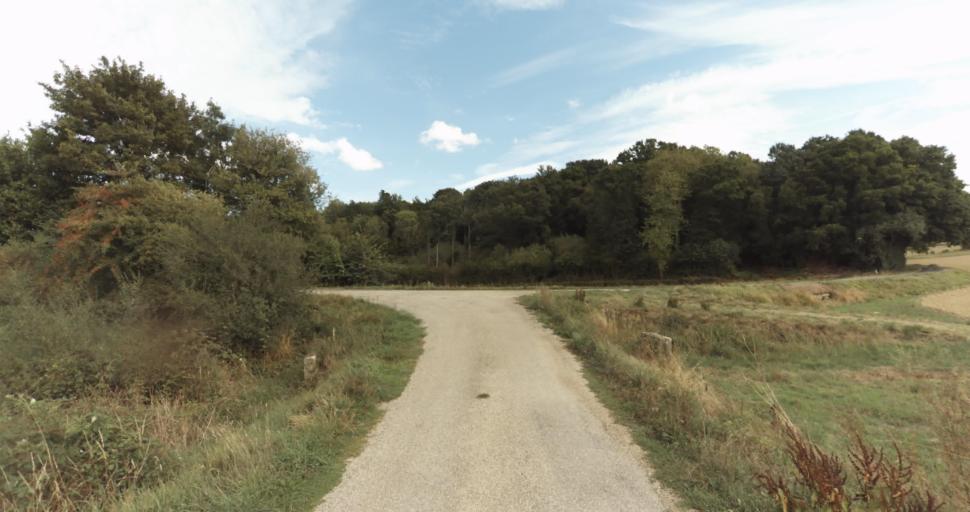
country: FR
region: Lower Normandy
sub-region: Departement du Calvados
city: Orbec
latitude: 48.9123
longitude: 0.3829
